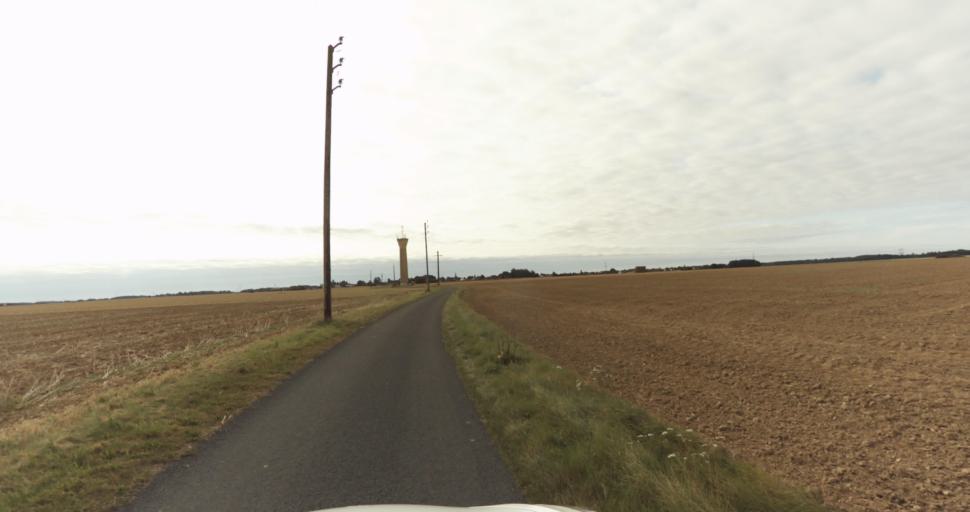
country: FR
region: Haute-Normandie
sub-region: Departement de l'Eure
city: La Madeleine-de-Nonancourt
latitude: 48.8744
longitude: 1.2362
